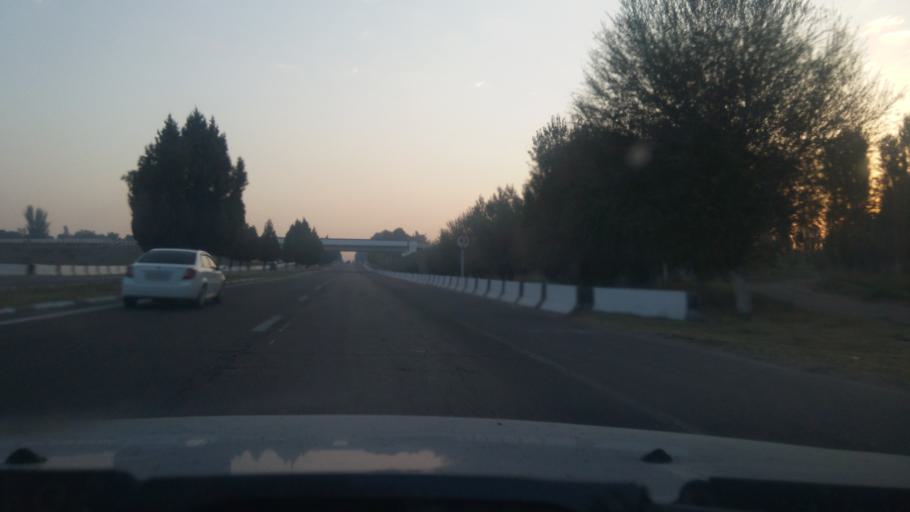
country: UZ
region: Toshkent
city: Amir Timur
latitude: 41.0826
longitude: 68.9412
